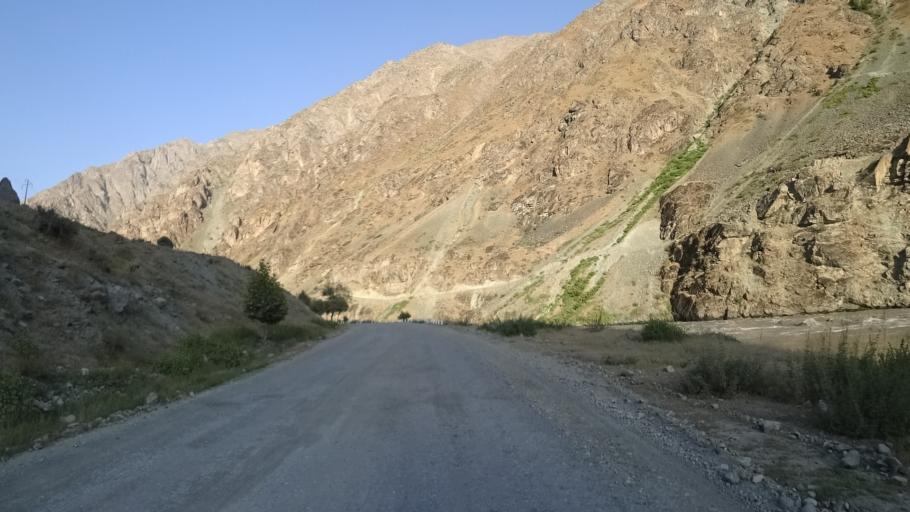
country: TJ
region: Gorno-Badakhshan
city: Qalaikhumb
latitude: 38.4172
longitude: 70.7330
